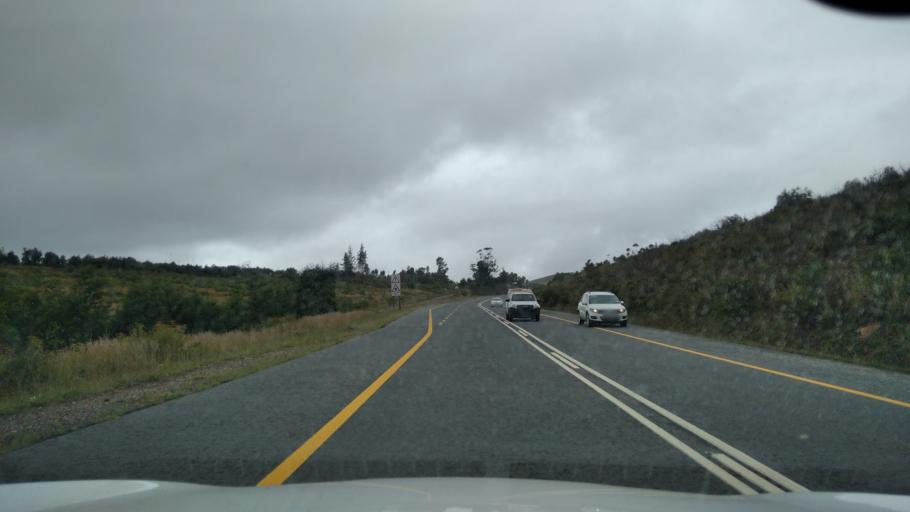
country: ZA
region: Western Cape
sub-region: Overberg District Municipality
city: Grabouw
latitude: -34.1911
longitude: 19.1249
